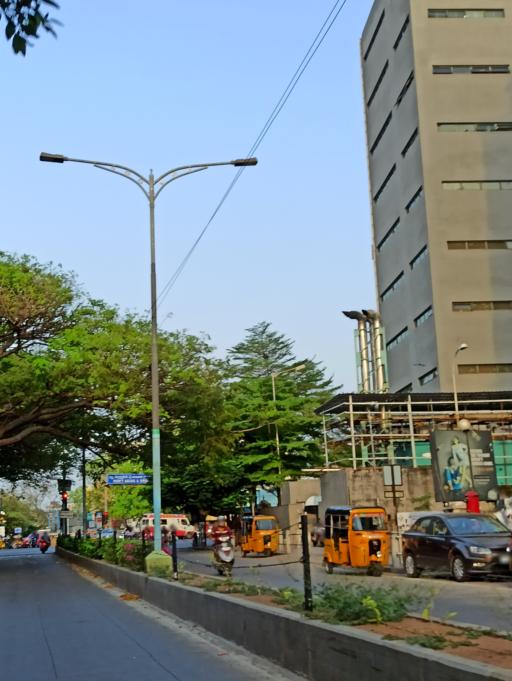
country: IN
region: Tamil Nadu
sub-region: Chennai
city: Chetput
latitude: 13.0693
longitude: 80.2416
